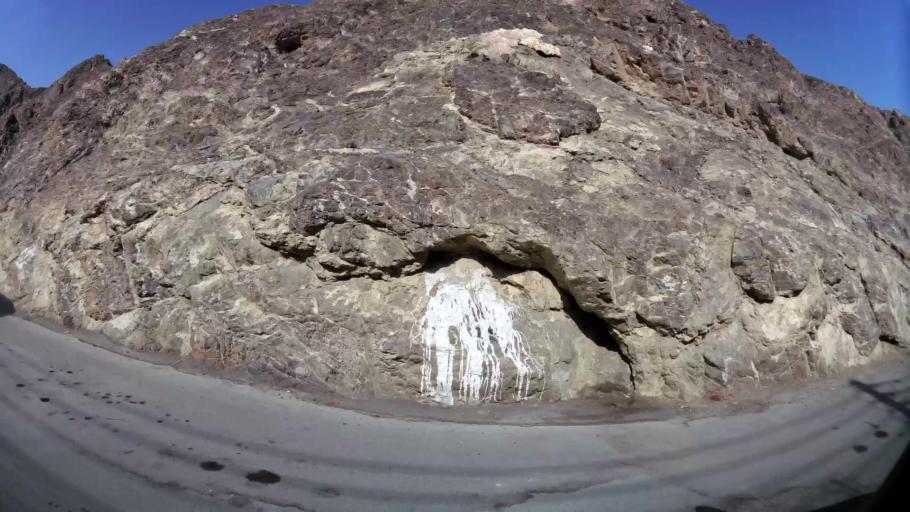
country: OM
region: Muhafazat Masqat
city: Muscat
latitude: 23.6028
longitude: 58.5548
